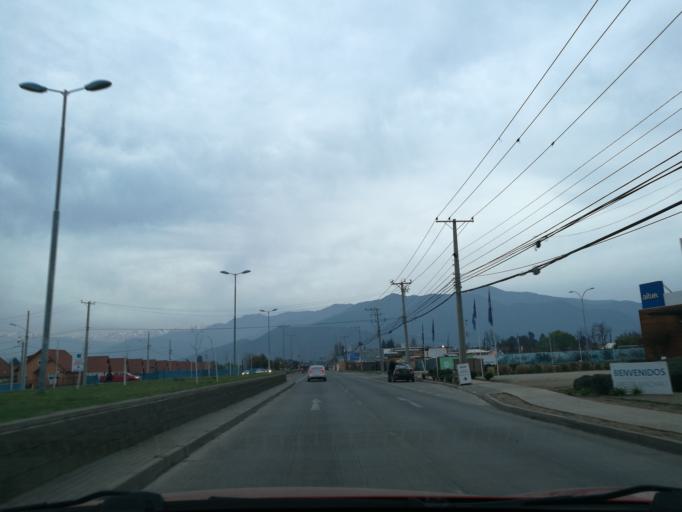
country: CL
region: O'Higgins
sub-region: Provincia de Cachapoal
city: Machali
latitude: -34.1700
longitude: -70.6790
